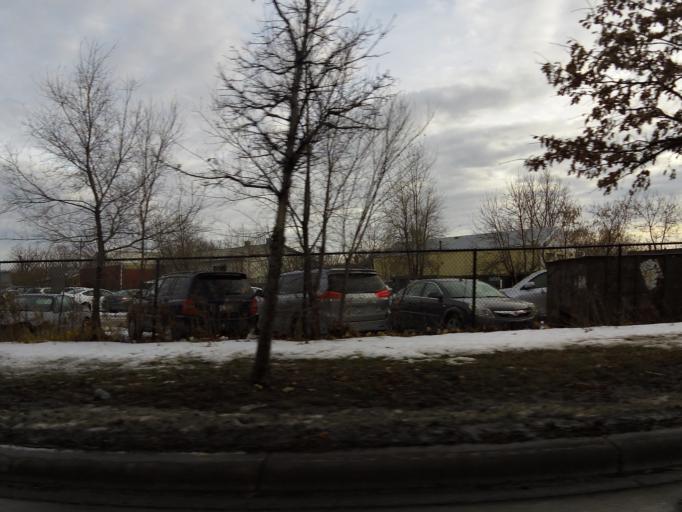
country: US
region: Minnesota
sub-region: Ramsey County
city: Saint Paul
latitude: 44.9685
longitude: -93.0506
